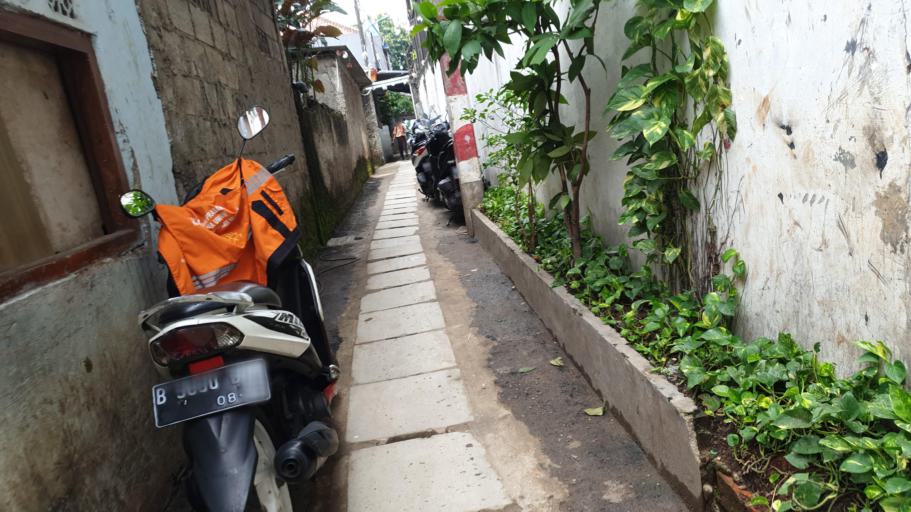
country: ID
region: Banten
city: South Tangerang
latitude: -6.2577
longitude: 106.7834
